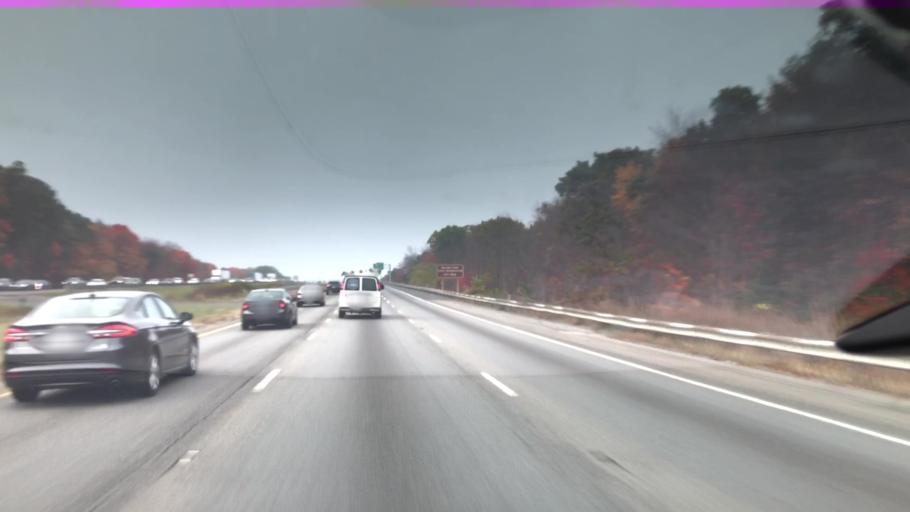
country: US
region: Massachusetts
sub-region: Middlesex County
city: Littleton Common
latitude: 42.5306
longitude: -71.5005
